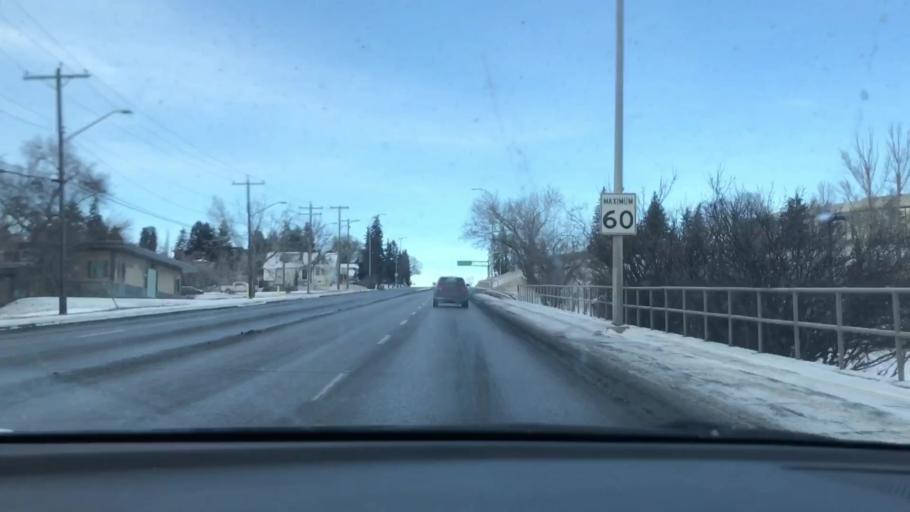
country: CA
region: Alberta
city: Calgary
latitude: 51.0599
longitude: -114.0947
